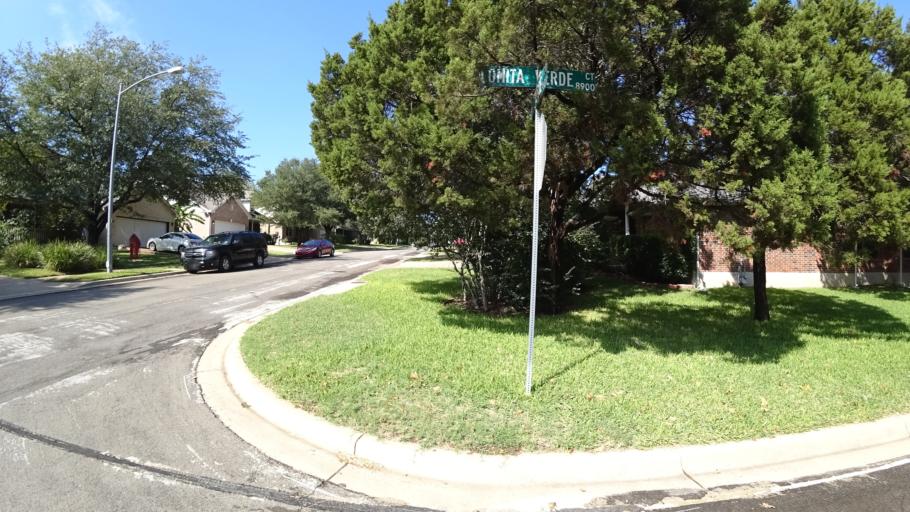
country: US
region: Texas
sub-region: Travis County
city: Shady Hollow
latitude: 30.2074
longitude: -97.8719
